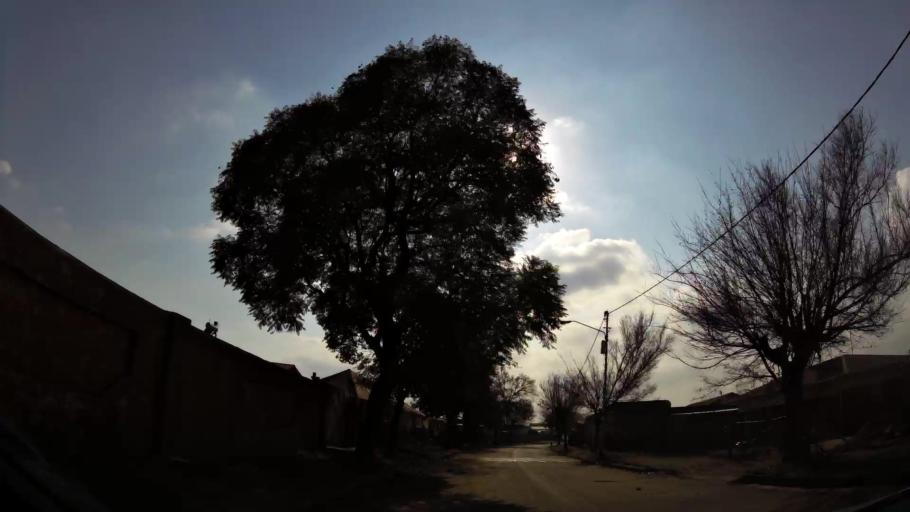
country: ZA
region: Gauteng
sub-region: City of Johannesburg Metropolitan Municipality
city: Modderfontein
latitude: -26.1582
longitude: 28.1996
